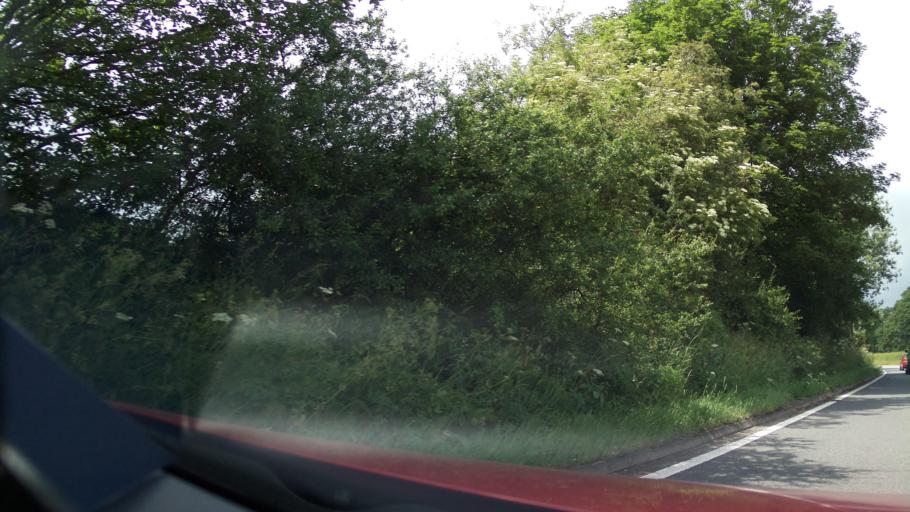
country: GB
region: England
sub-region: Derbyshire
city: Shirley
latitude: 52.9893
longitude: -1.6863
